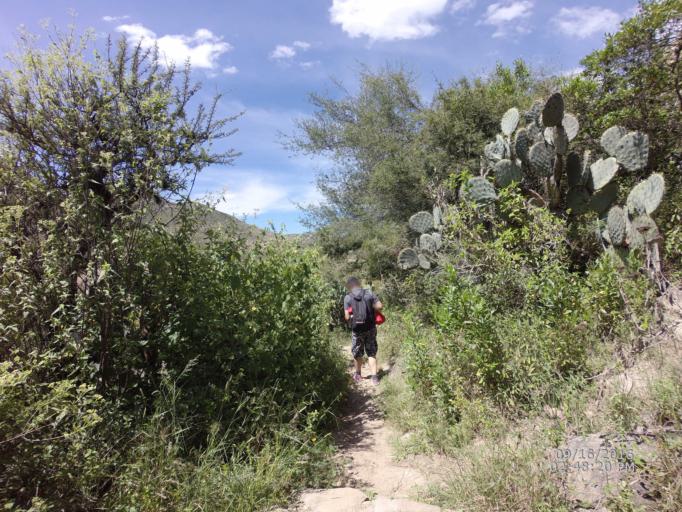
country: MX
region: Queretaro
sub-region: Ezequiel Montes
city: San Jose del Jagueey
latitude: 20.7509
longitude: -99.9495
